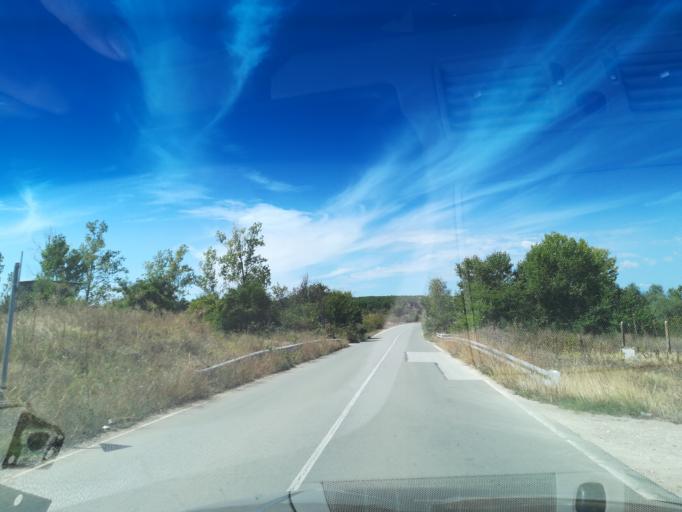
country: BG
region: Plovdiv
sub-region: Obshtina Suedinenie
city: Suedinenie
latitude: 42.3826
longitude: 24.5792
